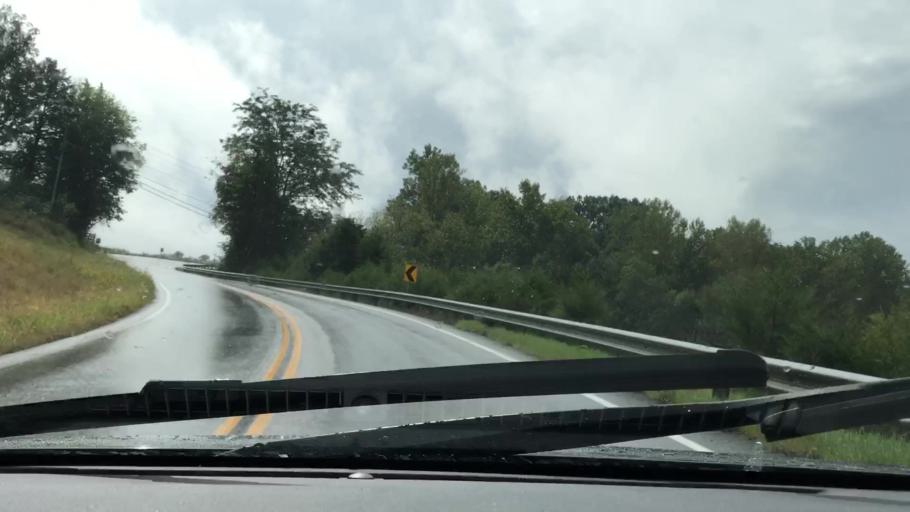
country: US
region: Kentucky
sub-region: Monroe County
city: Tompkinsville
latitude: 36.6382
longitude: -85.7669
